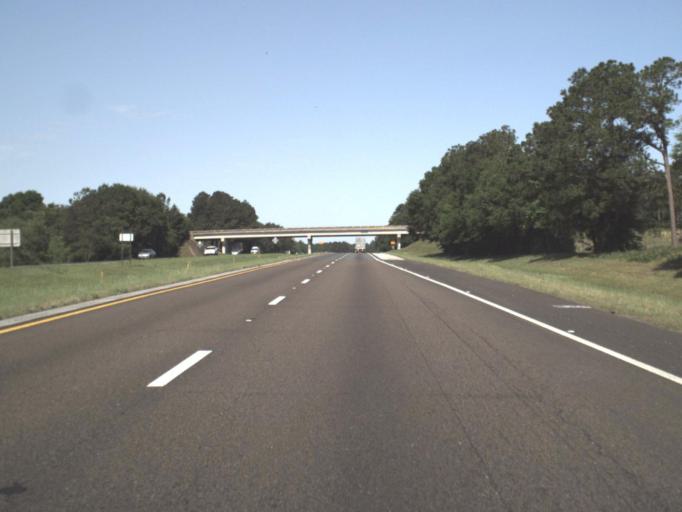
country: US
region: Florida
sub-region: Holmes County
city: Bonifay
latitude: 30.7631
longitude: -85.6929
